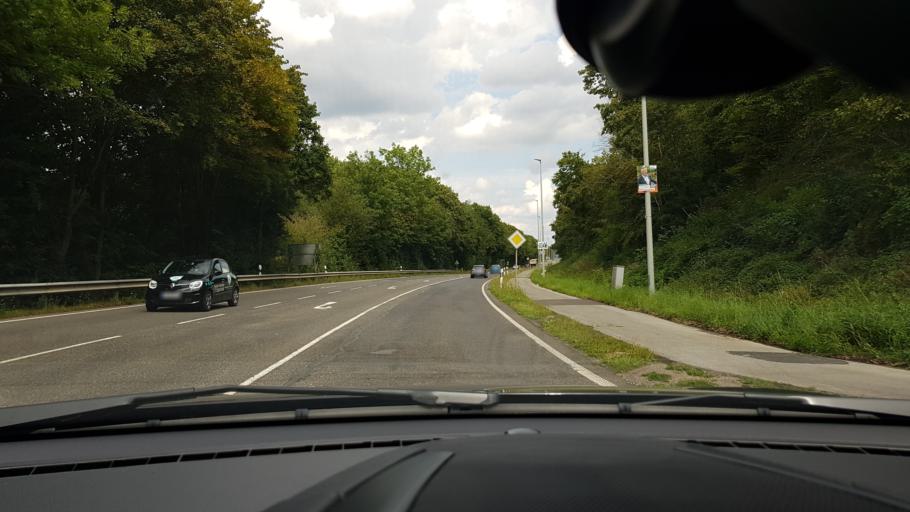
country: DE
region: North Rhine-Westphalia
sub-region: Regierungsbezirk Dusseldorf
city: Grevenbroich
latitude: 51.0677
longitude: 6.5827
